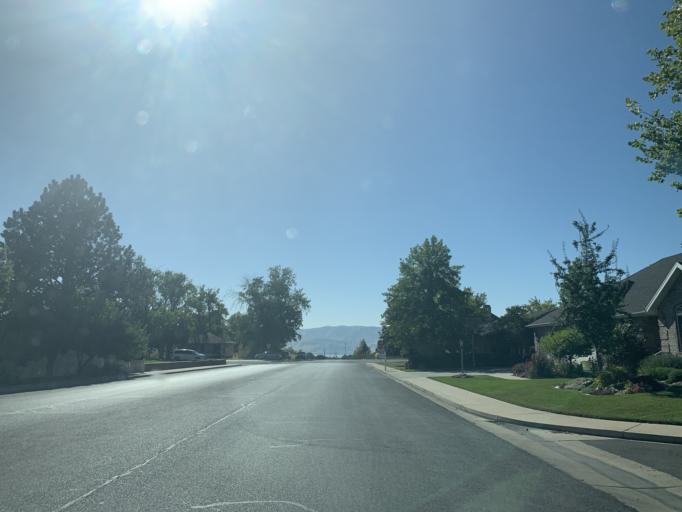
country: US
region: Utah
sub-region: Utah County
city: Orem
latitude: 40.2571
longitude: -111.6938
